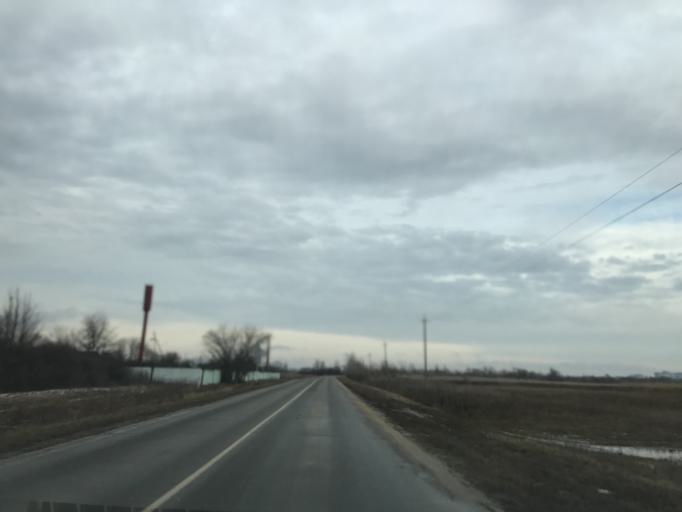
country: RU
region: Rostov
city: Glubokiy
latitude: 48.4770
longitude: 40.3053
